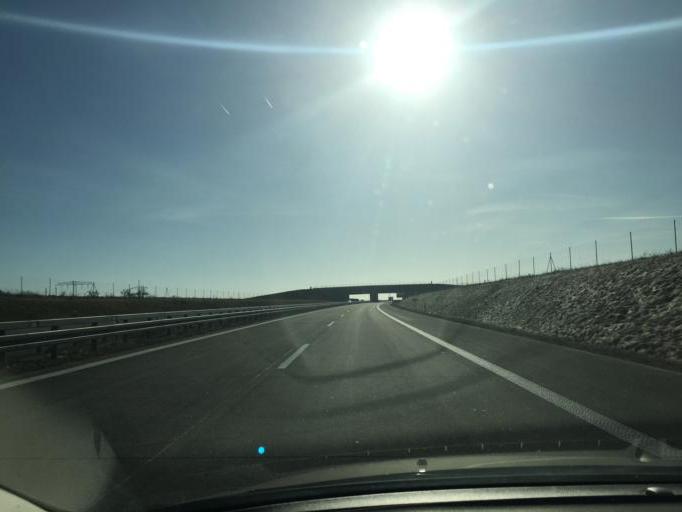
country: DE
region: Saxony
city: Frohburg
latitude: 51.0768
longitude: 12.5916
